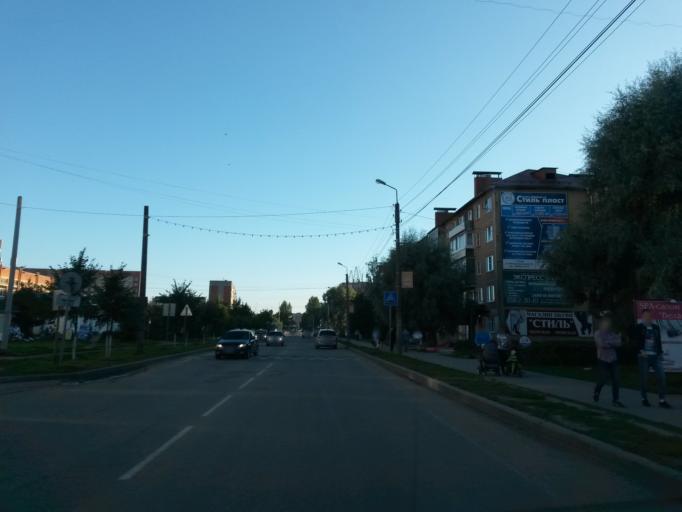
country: RU
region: Jaroslavl
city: Tutayev
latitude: 57.8660
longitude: 39.5149
